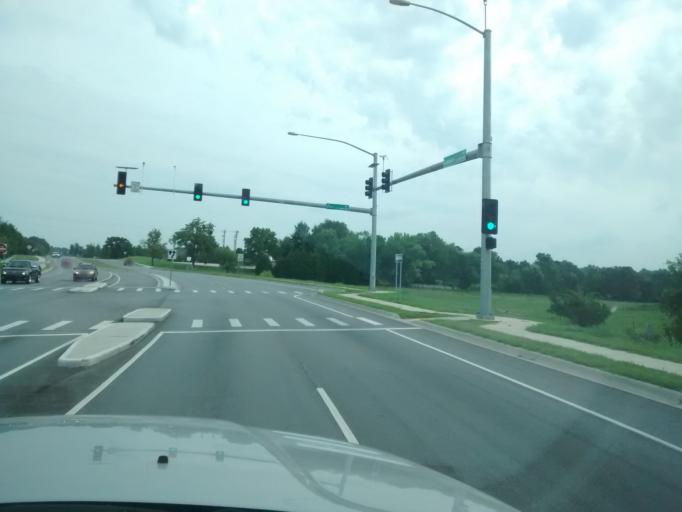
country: US
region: Arkansas
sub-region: Washington County
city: Johnson
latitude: 36.1290
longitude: -94.1180
